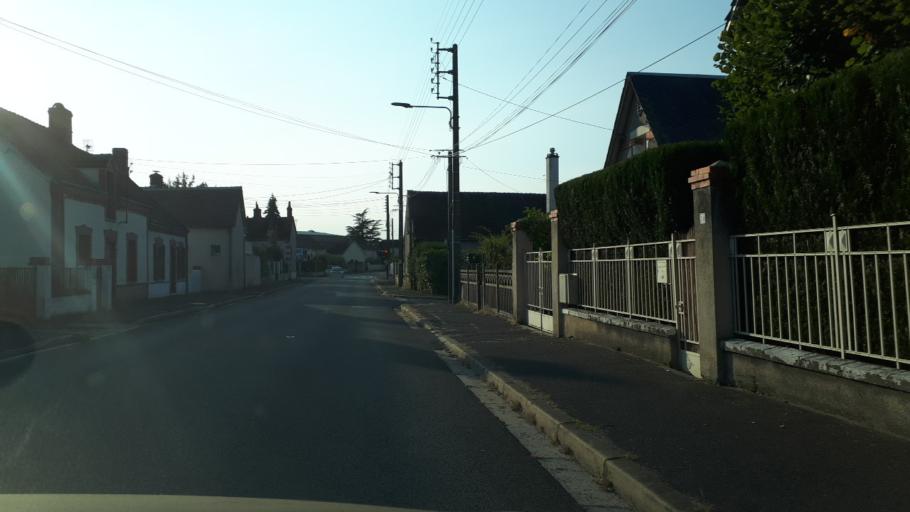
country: FR
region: Centre
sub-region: Departement du Loir-et-Cher
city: Romorantin-Lanthenay
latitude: 47.3520
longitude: 1.7509
